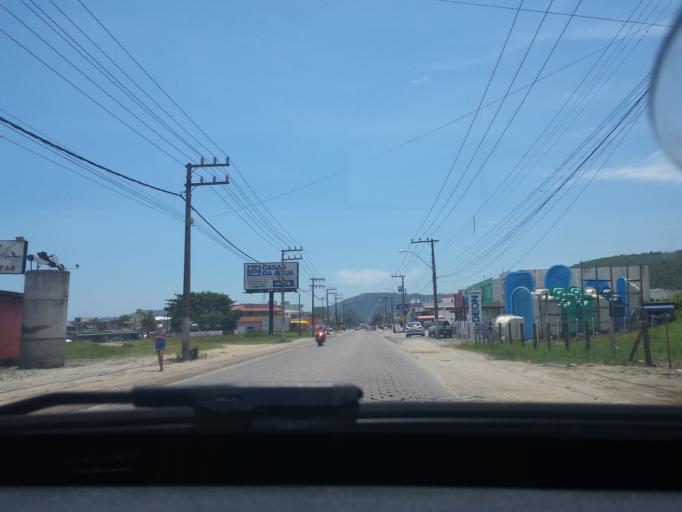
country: BR
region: Santa Catarina
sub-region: Porto Belo
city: Porto Belo
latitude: -27.1602
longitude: -48.5733
